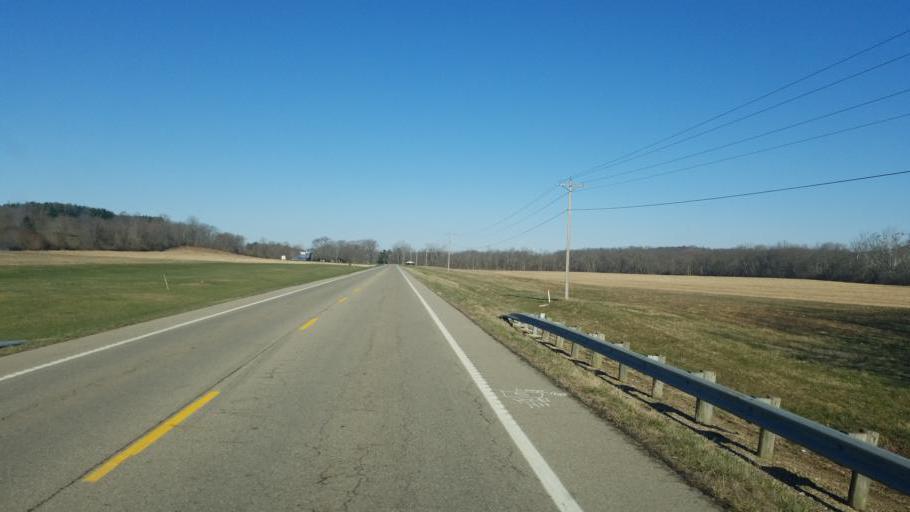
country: US
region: Ohio
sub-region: Highland County
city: Greenfield
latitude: 39.2269
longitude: -83.3174
